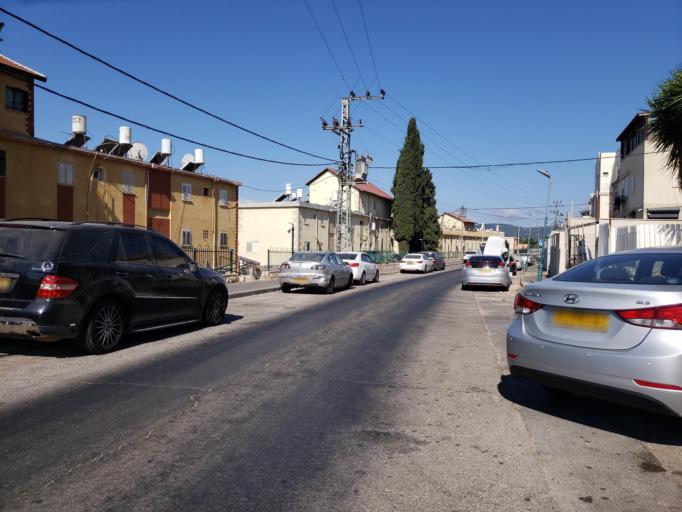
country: IL
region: Northern District
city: Safed
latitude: 32.9562
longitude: 35.4970
